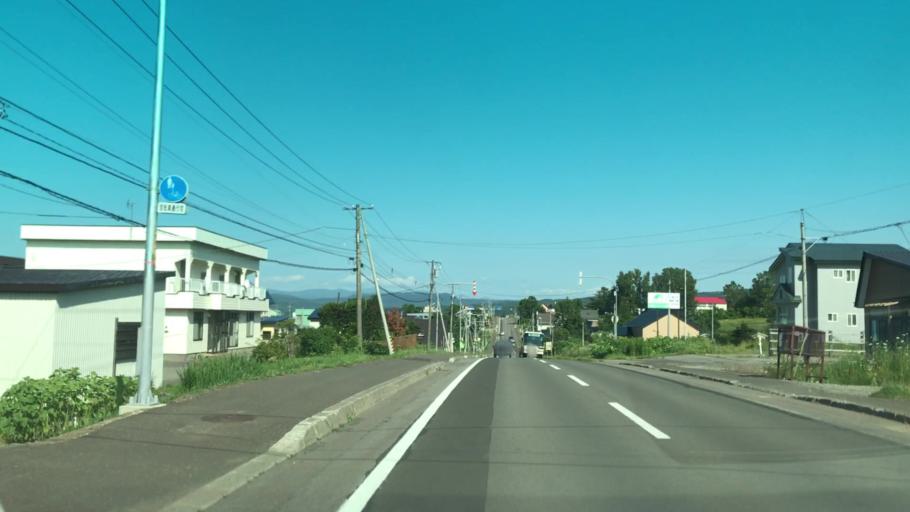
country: JP
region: Hokkaido
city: Iwanai
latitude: 42.9832
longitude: 140.5652
